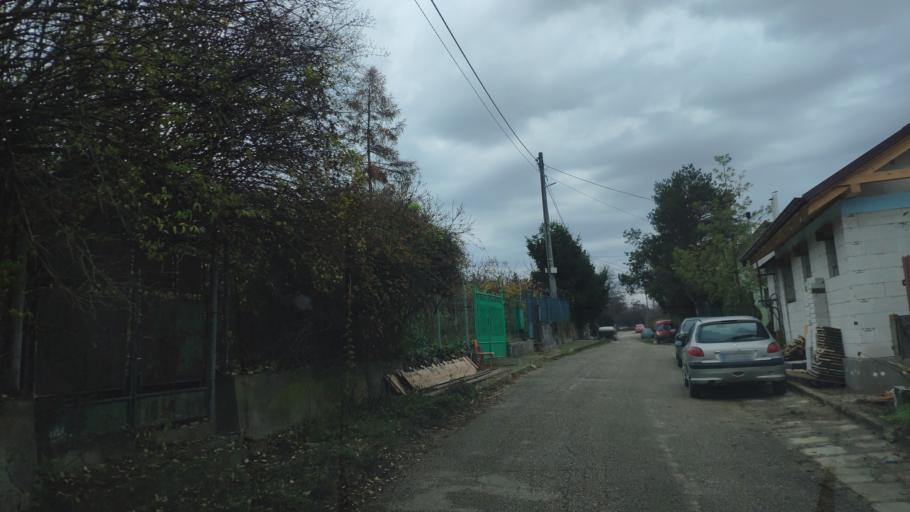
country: SK
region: Kosicky
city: Kosice
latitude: 48.6990
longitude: 21.2878
